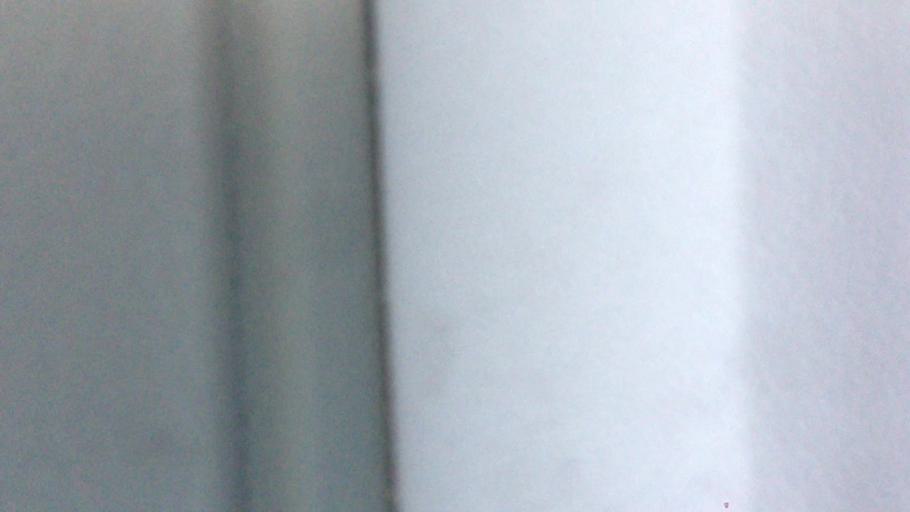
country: US
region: New York
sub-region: Dutchess County
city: Rhinebeck
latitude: 41.9718
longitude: -73.9208
